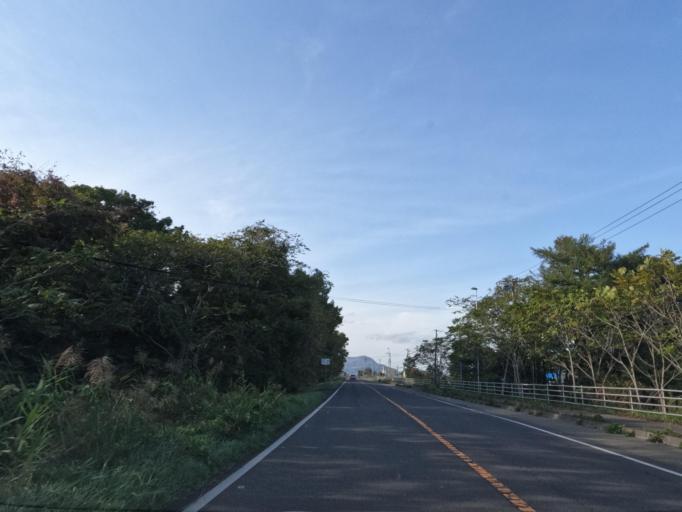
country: JP
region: Hokkaido
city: Date
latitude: 42.4249
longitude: 140.9067
